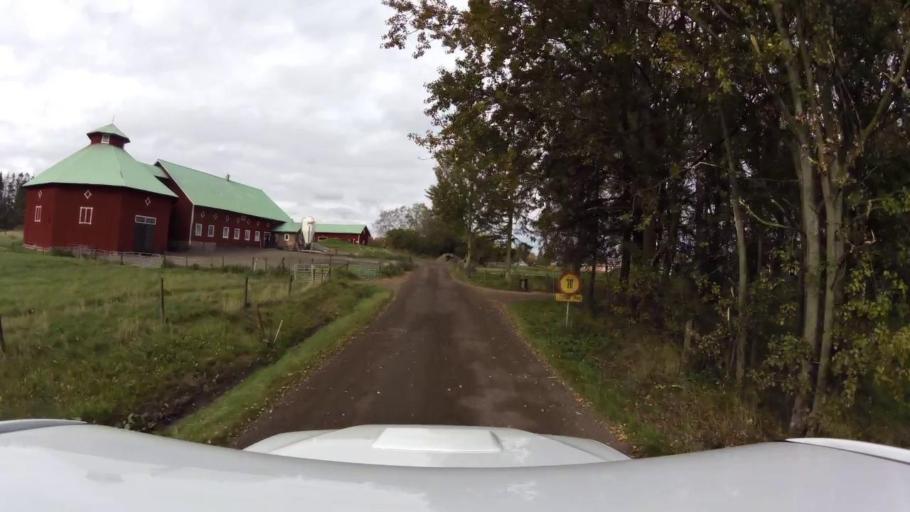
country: SE
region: OEstergoetland
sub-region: Linkopings Kommun
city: Ekangen
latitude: 58.4476
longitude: 15.5868
